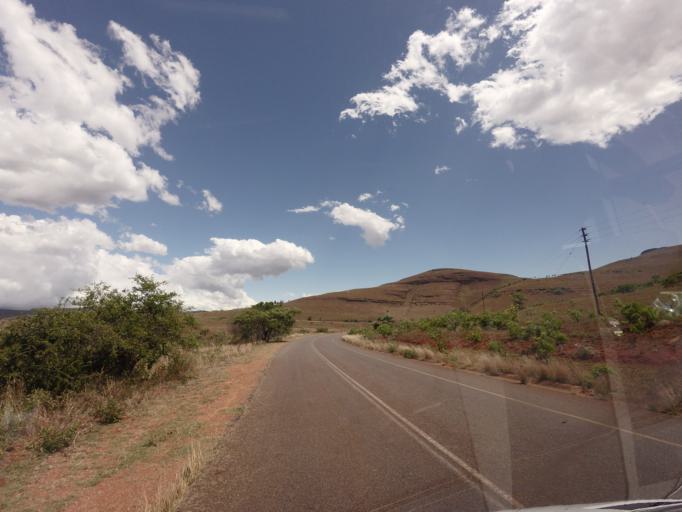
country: ZA
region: Mpumalanga
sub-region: Ehlanzeni District
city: Graksop
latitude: -24.6325
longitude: 30.8118
